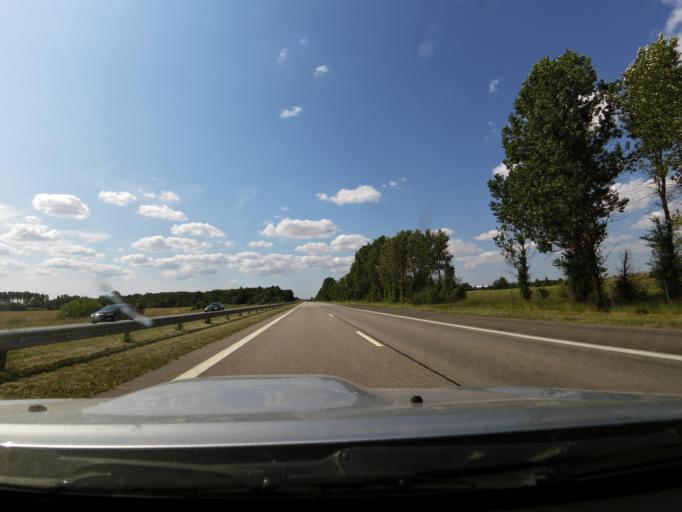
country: LT
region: Klaipedos apskritis
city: Gargzdai
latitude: 55.7085
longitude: 21.5242
